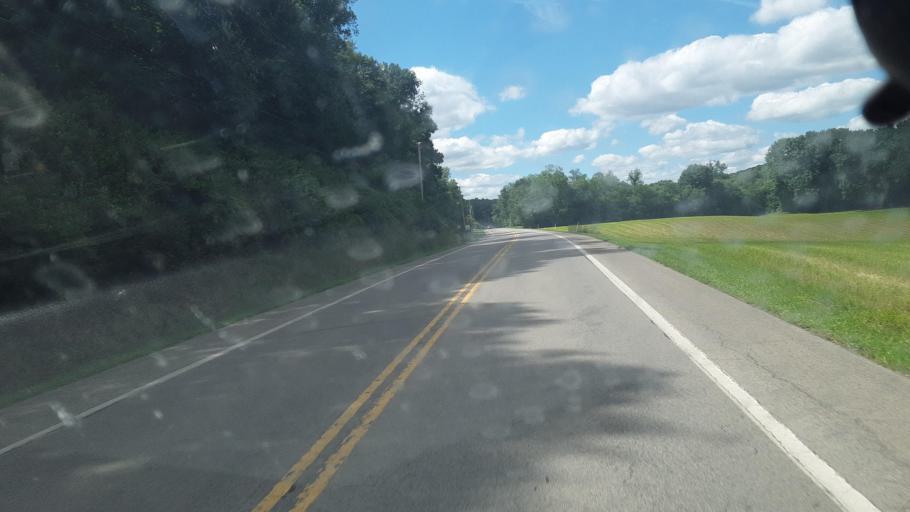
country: US
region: Pennsylvania
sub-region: Butler County
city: Slippery Rock
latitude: 41.0138
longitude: -80.1798
